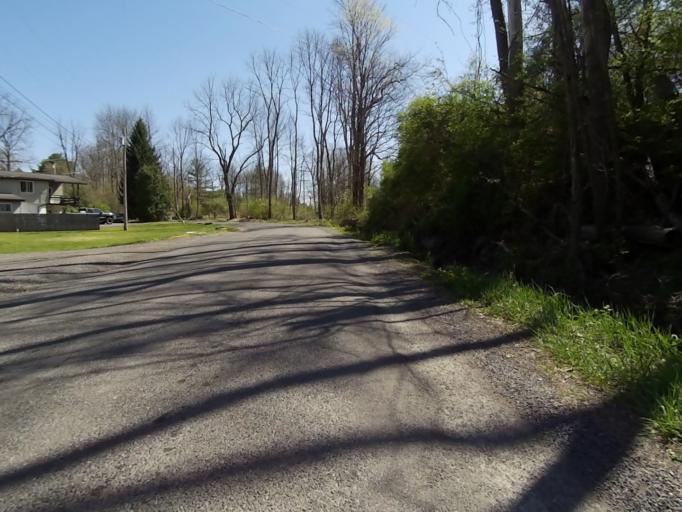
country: US
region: Pennsylvania
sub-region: Centre County
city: Houserville
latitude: 40.8837
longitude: -77.8393
